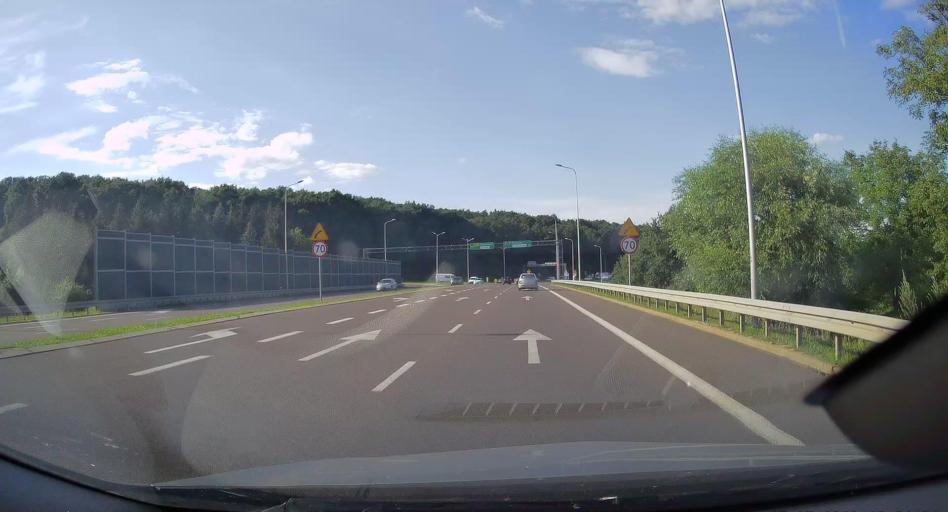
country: PL
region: Subcarpathian Voivodeship
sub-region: Powiat przemyski
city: Zurawica
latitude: 49.8075
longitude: 22.7775
